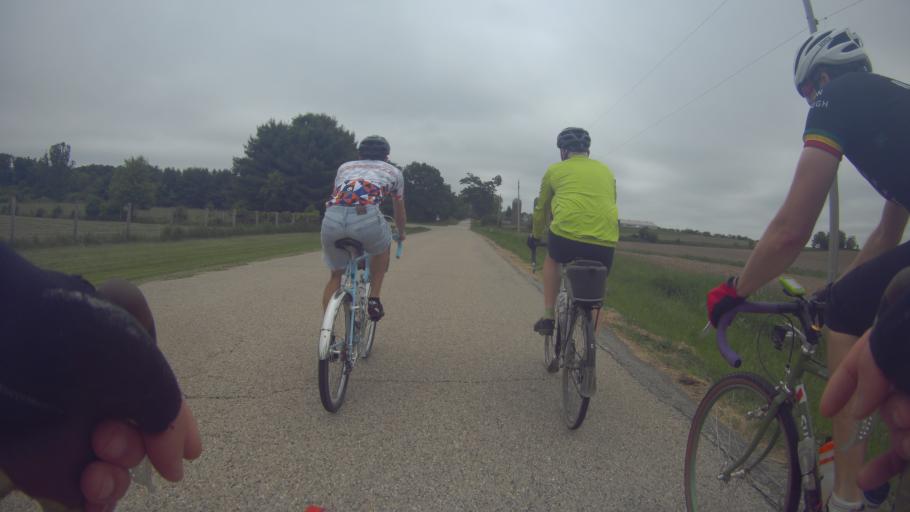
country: US
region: Wisconsin
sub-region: Green County
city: Brooklyn
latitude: 42.8781
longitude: -89.3905
